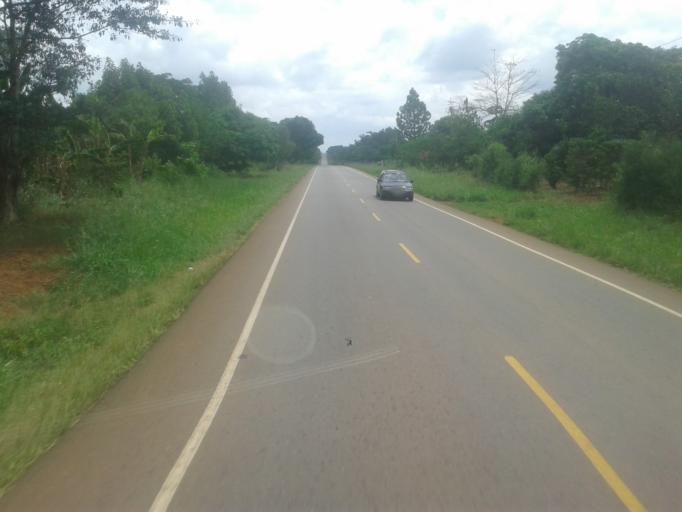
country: UG
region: Central Region
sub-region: Nakasongola District
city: Nakasongola
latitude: 1.0867
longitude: 32.4663
